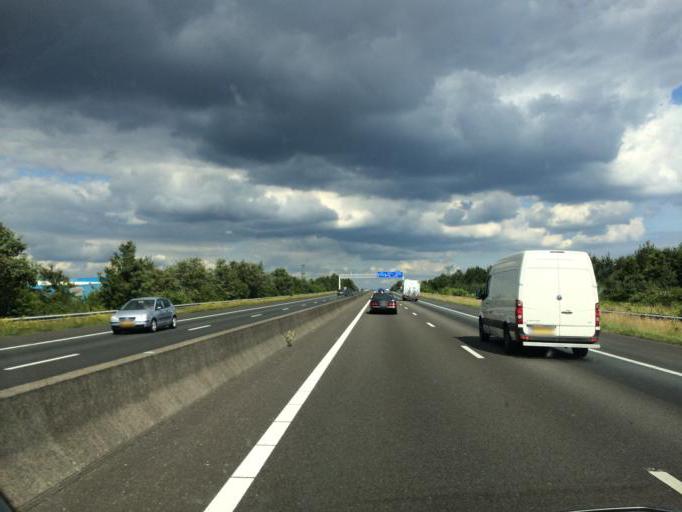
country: NL
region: Limburg
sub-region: Gemeente Venlo
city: Tegelen
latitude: 51.3938
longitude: 6.1036
